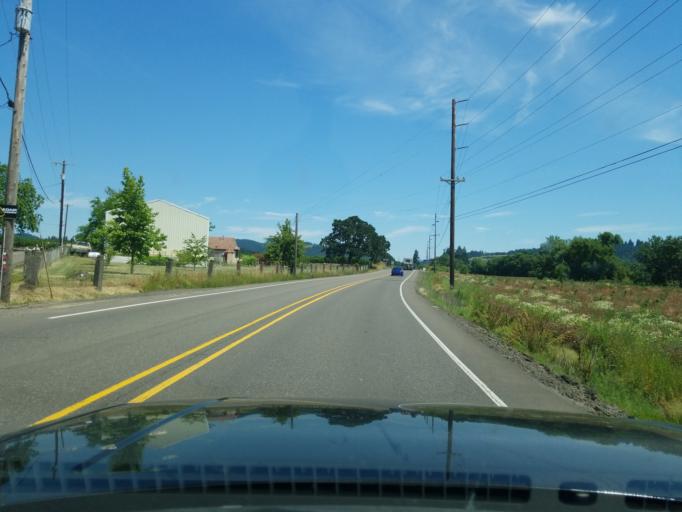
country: US
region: Oregon
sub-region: Yamhill County
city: Yamhill
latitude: 45.3503
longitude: -123.1750
